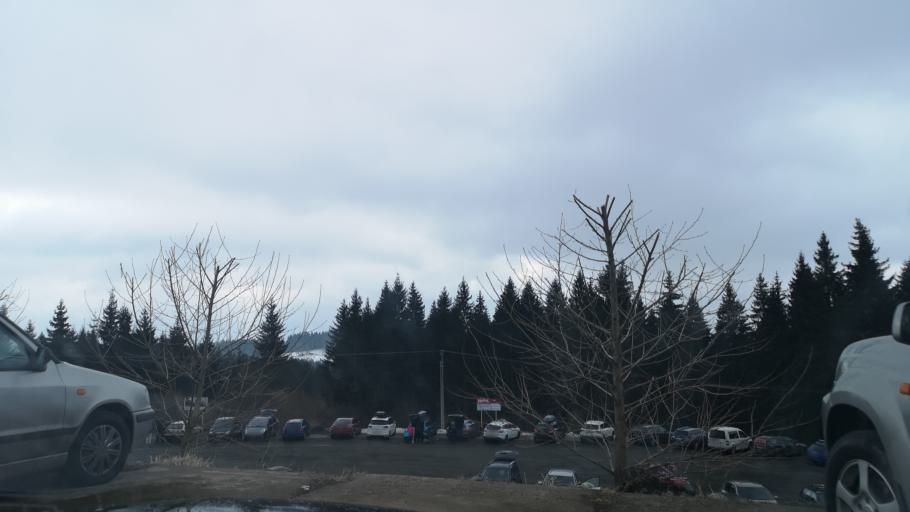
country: SK
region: Zilinsky
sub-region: Okres Dolny Kubin
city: Dolny Kubin
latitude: 49.2509
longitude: 19.2683
